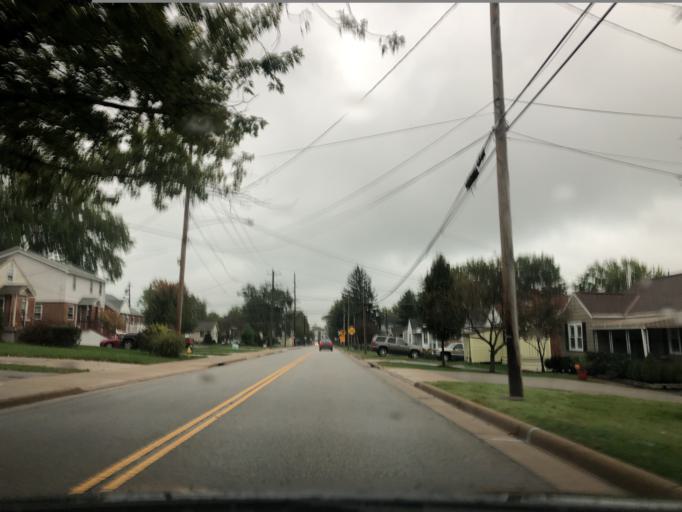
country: US
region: Ohio
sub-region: Hamilton County
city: Blue Ash
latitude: 39.2291
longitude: -84.3823
